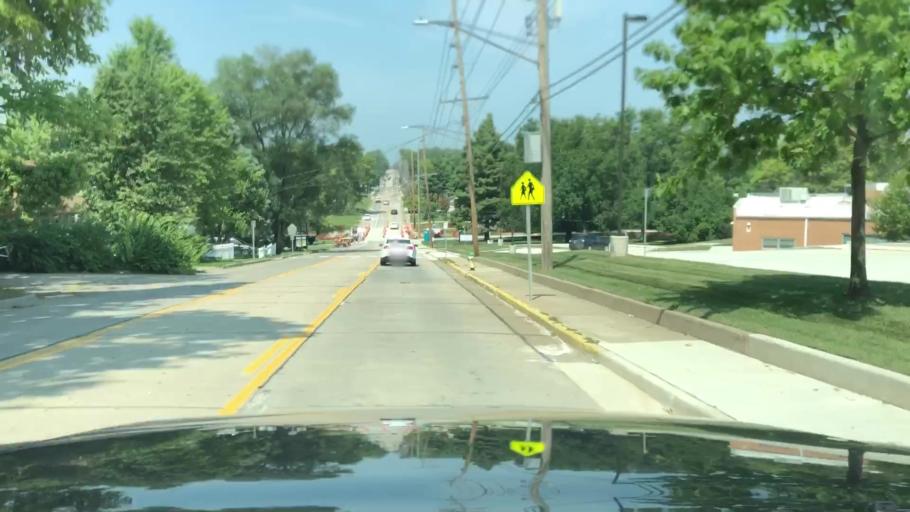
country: US
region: Missouri
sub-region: Saint Charles County
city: Saint Charles
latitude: 38.7919
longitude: -90.4969
